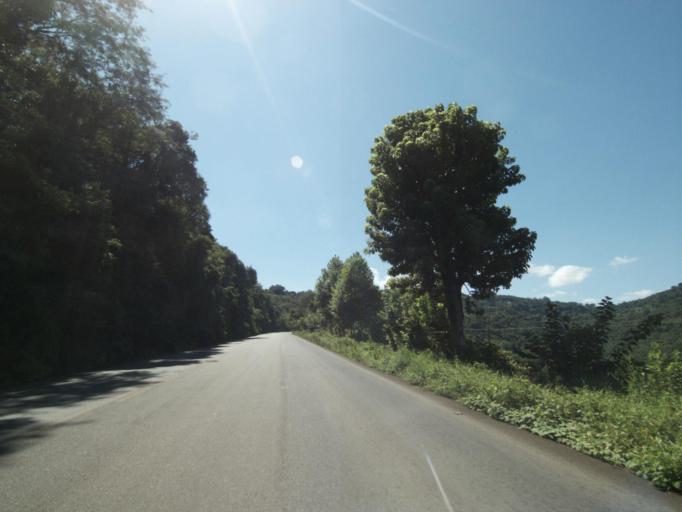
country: BR
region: Rio Grande do Sul
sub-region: Bento Goncalves
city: Bento Goncalves
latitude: -29.1000
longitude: -51.6160
